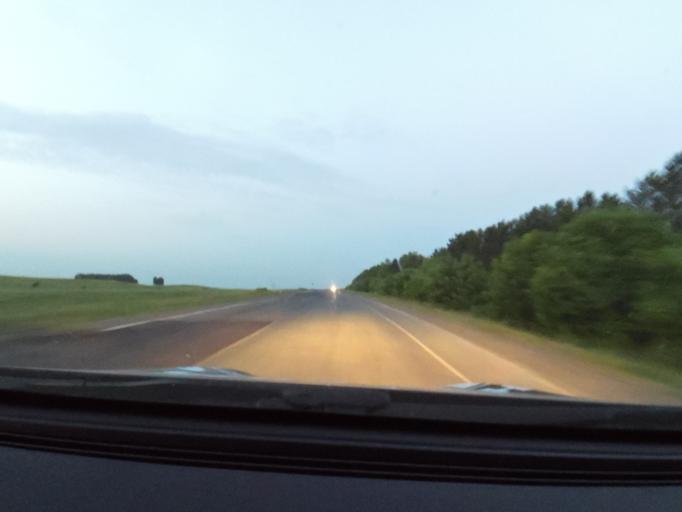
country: RU
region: Bashkortostan
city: Duvan
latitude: 56.0776
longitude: 58.0928
